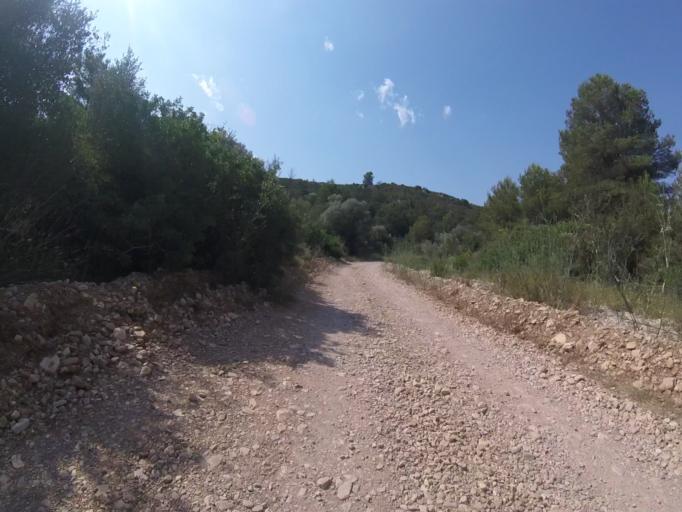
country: ES
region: Valencia
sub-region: Provincia de Castello
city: Cuevas de Vinroma
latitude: 40.3040
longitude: 0.1699
